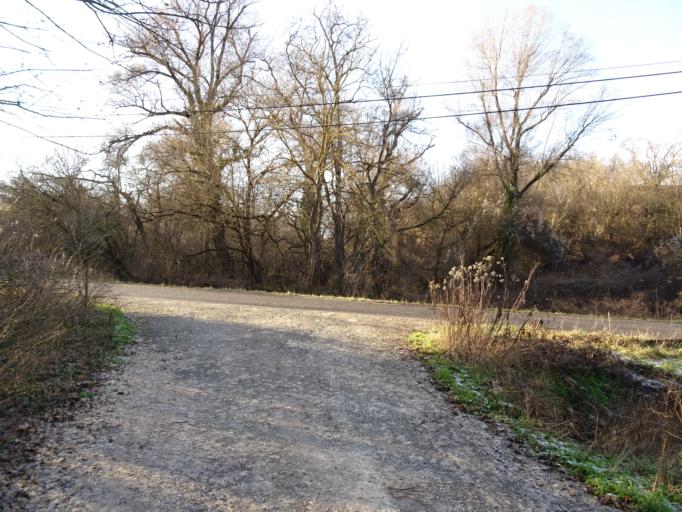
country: HU
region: Pest
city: Uri
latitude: 47.3993
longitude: 19.4916
